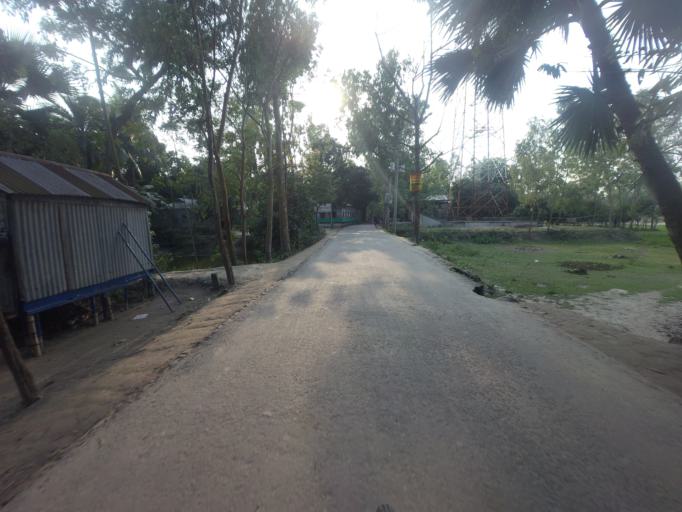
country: BD
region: Rajshahi
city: Sirajganj
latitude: 24.3184
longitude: 89.6968
